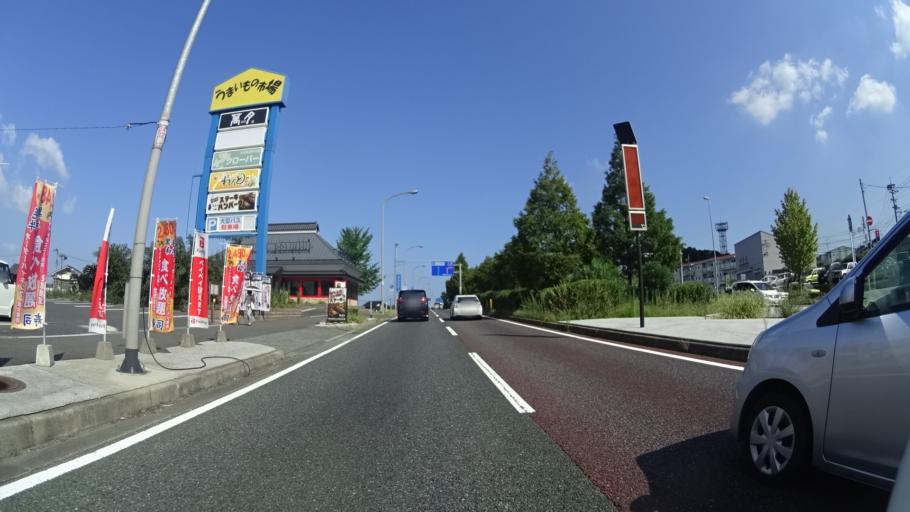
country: JP
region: Fukuoka
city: Kanda
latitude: 33.8108
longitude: 130.9484
